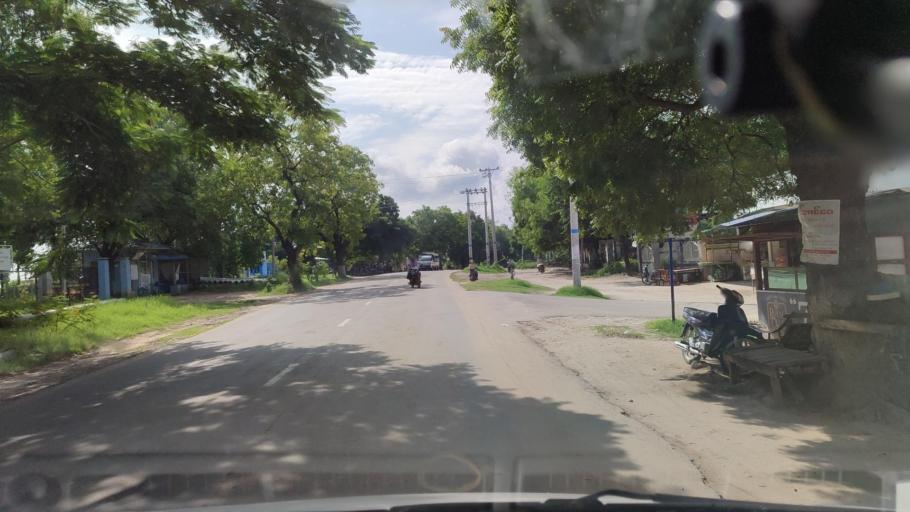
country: MM
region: Mandalay
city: Meiktila
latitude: 21.0986
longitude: 95.6509
